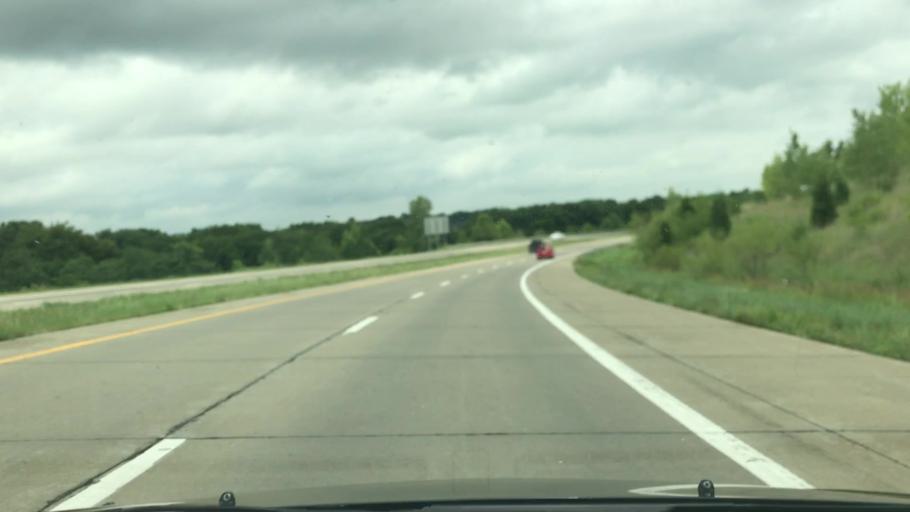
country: US
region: Missouri
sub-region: Jackson County
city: Grandview
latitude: 38.8647
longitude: -94.5989
